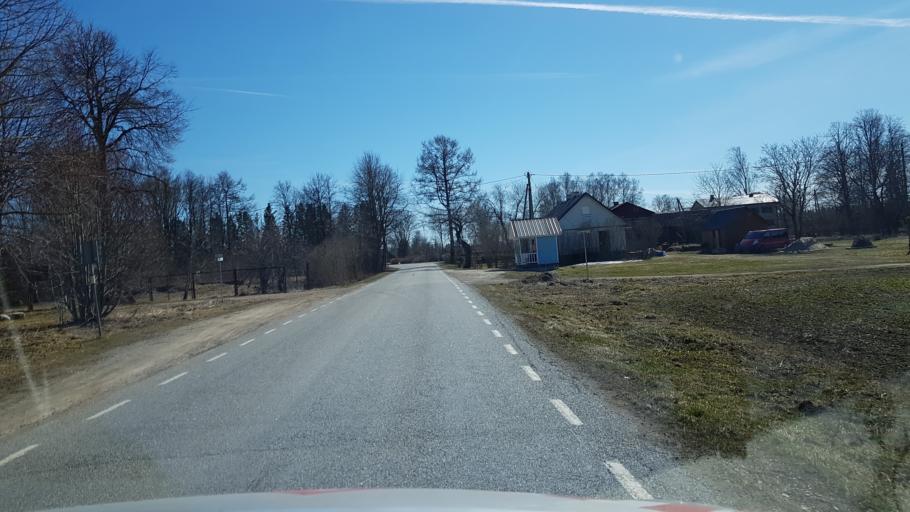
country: EE
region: Laeaene-Virumaa
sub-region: Viru-Nigula vald
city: Kunda
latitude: 59.3467
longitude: 26.6757
